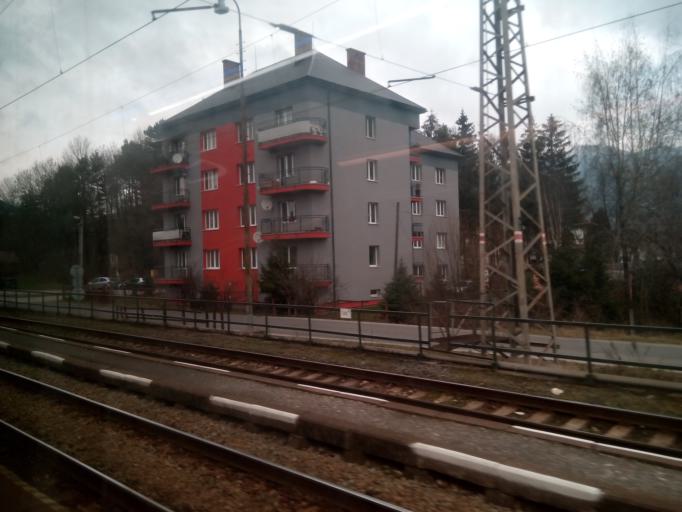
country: SK
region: Zilinsky
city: Ruzomberok
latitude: 49.0838
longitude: 19.3089
